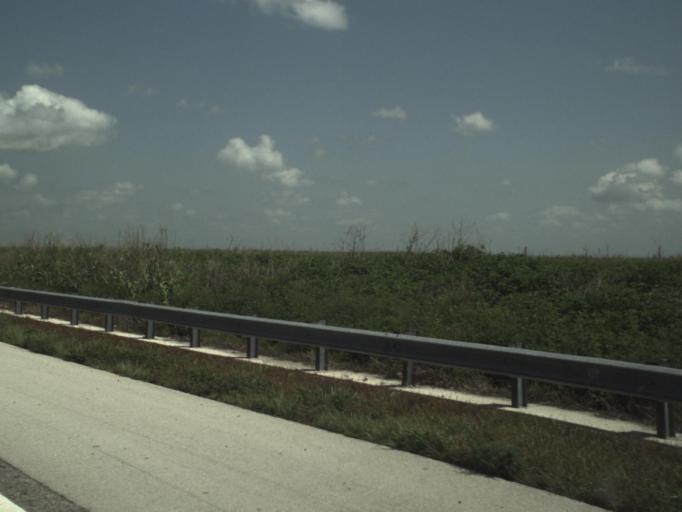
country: US
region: Florida
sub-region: Palm Beach County
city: Belle Glade Camp
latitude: 26.3797
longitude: -80.5723
